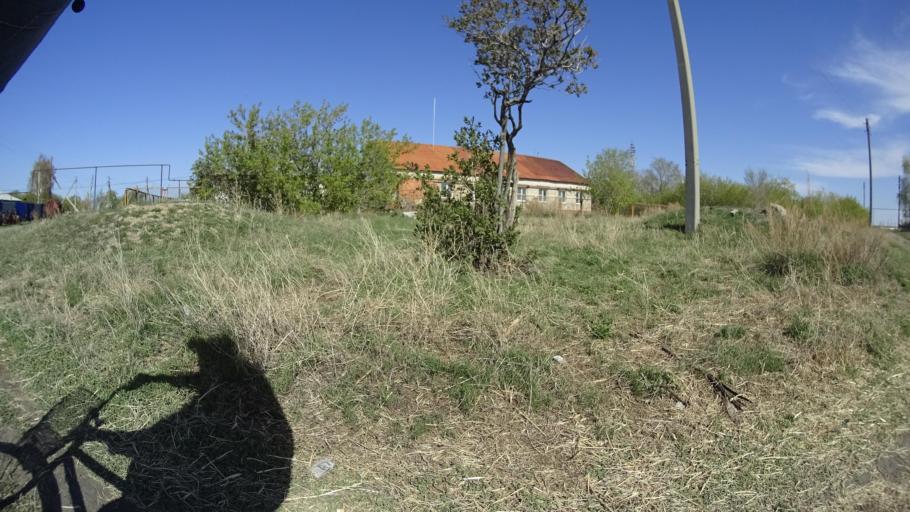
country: RU
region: Chelyabinsk
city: Chesma
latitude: 53.7912
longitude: 61.0356
